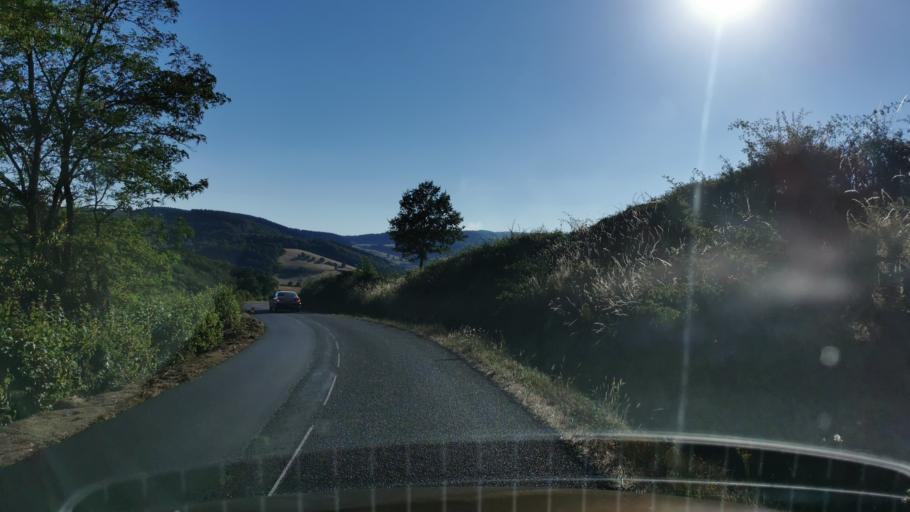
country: FR
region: Bourgogne
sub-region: Departement de Saone-et-Loire
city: Marmagne
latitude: 46.8031
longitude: 4.3487
